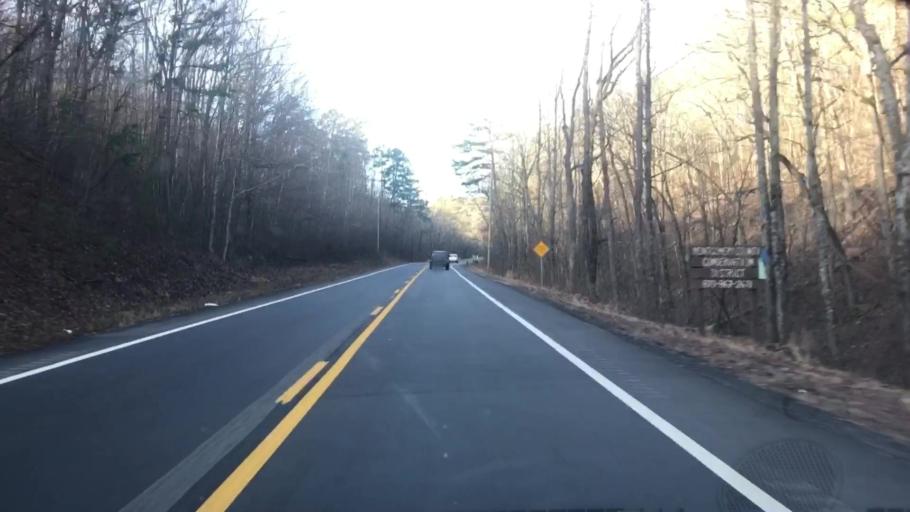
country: US
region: Arkansas
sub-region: Montgomery County
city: Mount Ida
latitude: 34.5240
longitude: -93.4061
